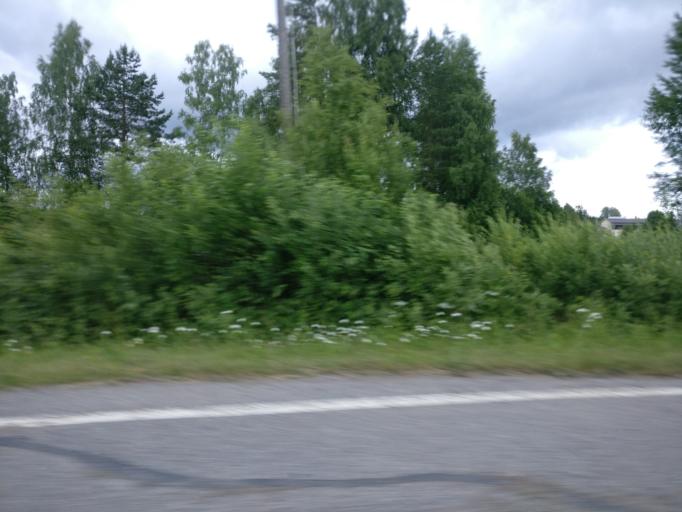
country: FI
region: Northern Savo
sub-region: Varkaus
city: Kangaslampi
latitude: 62.1597
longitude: 28.1526
